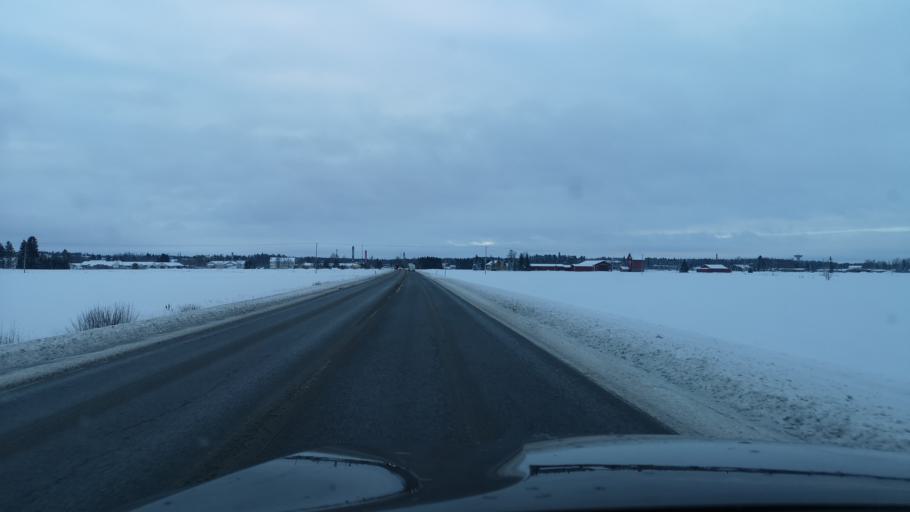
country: FI
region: Varsinais-Suomi
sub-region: Loimaa
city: Loimaa
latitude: 60.8654
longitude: 23.0530
